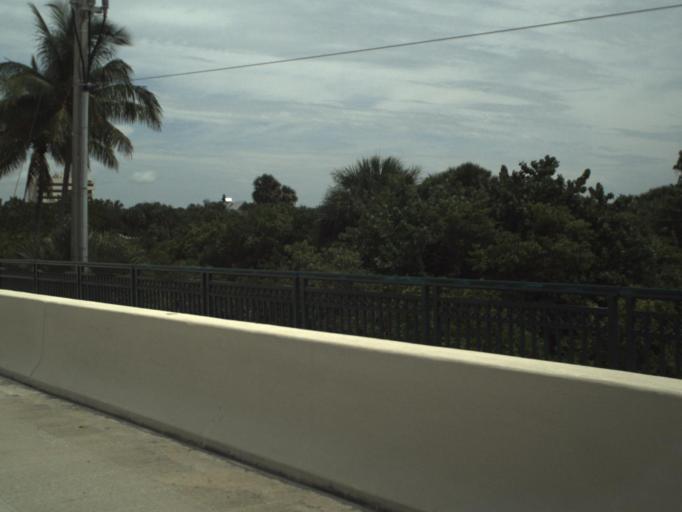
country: US
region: Florida
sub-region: Palm Beach County
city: Jupiter
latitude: 26.9377
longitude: -80.0828
